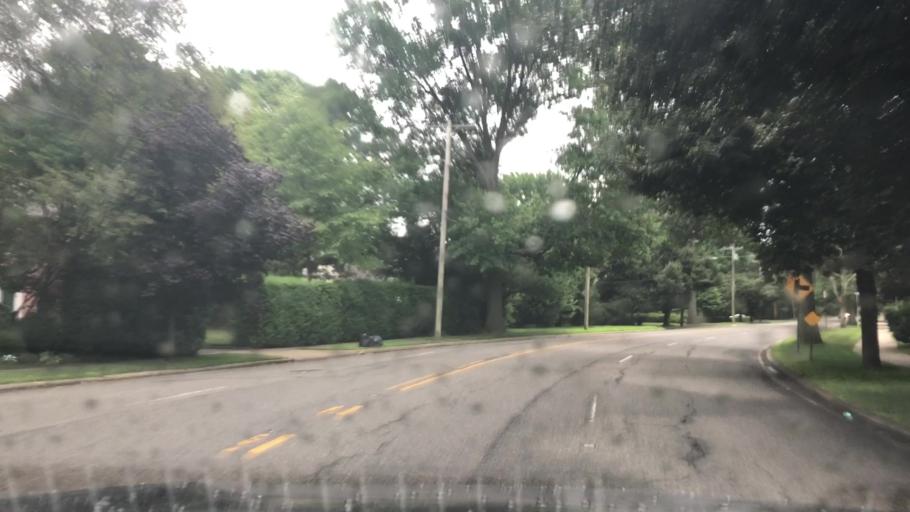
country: US
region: New York
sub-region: Nassau County
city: Garden City
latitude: 40.7135
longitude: -73.6374
